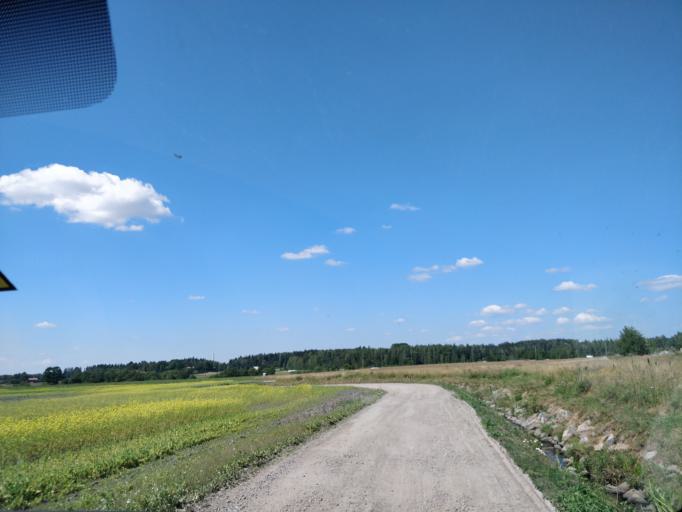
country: FI
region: Uusimaa
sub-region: Helsinki
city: Vantaa
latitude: 60.3106
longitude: 25.0912
